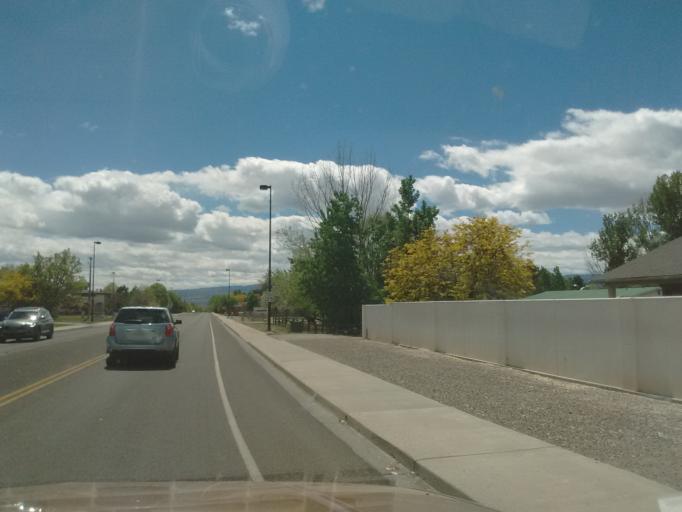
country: US
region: Colorado
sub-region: Mesa County
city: Grand Junction
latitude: 39.1040
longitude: -108.5431
